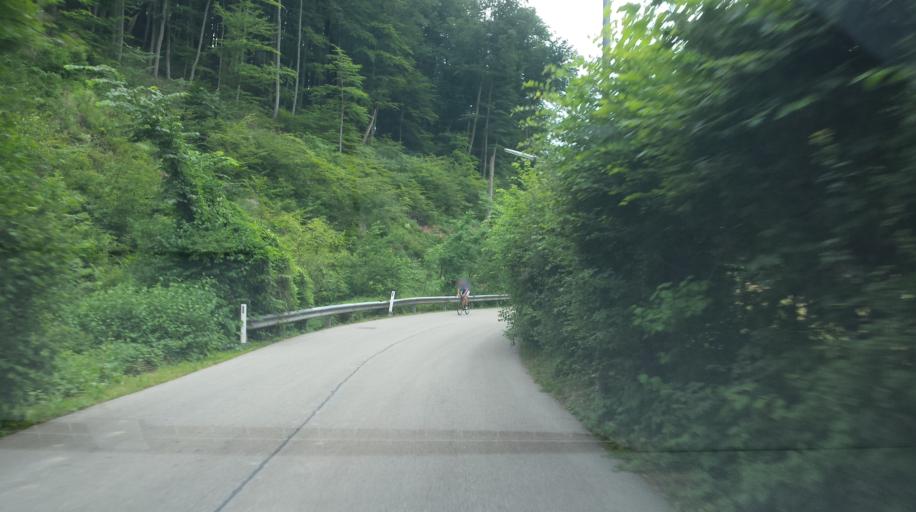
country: AT
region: Lower Austria
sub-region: Politischer Bezirk Wien-Umgebung
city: Mauerbach
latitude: 48.2402
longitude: 16.2060
